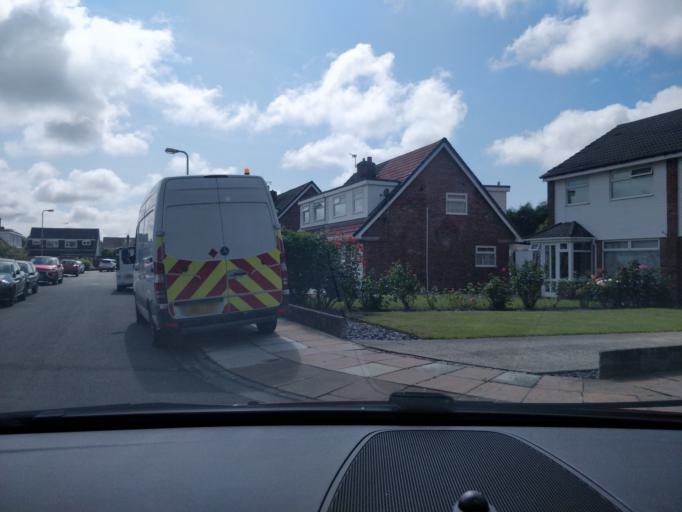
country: GB
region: England
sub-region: Lancashire
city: Banks
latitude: 53.6760
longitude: -2.9572
